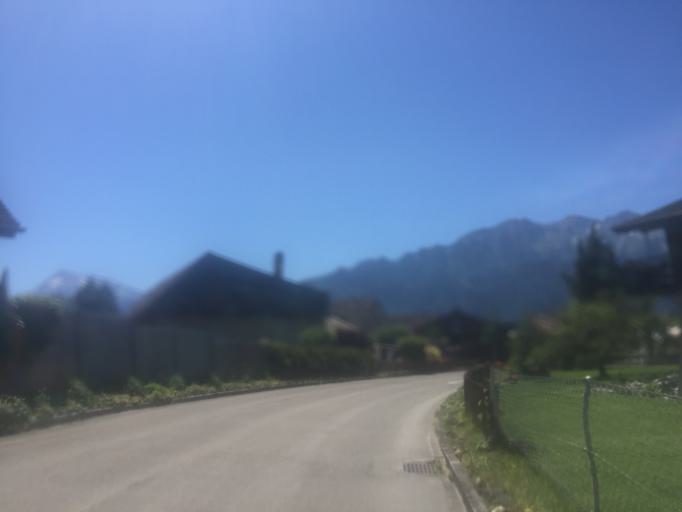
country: CH
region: Bern
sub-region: Thun District
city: Thierachern
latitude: 46.7452
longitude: 7.5935
